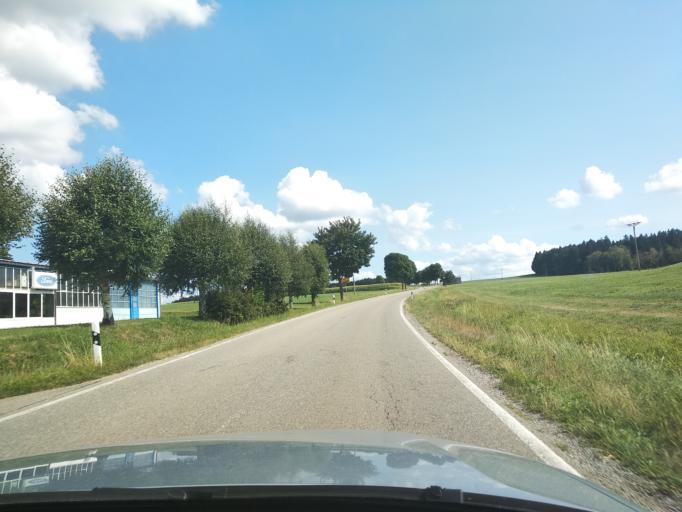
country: DE
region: Baden-Wuerttemberg
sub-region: Tuebingen Region
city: Leutkirch im Allgau
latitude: 47.8879
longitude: 9.9777
